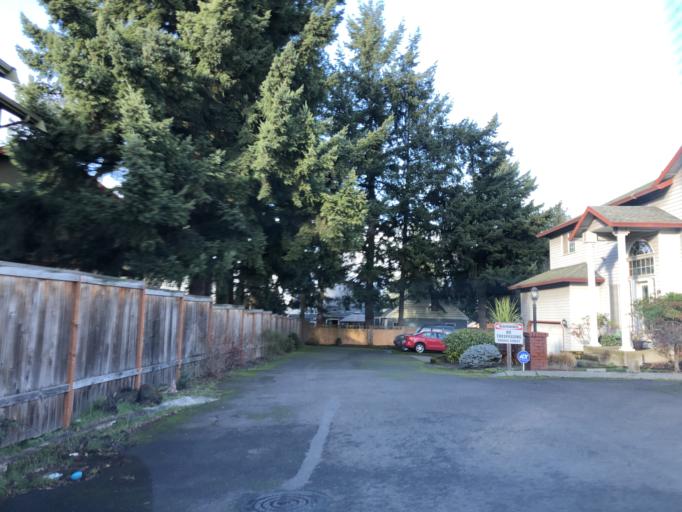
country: US
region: Oregon
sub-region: Multnomah County
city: Portland
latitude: 45.5577
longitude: -122.6130
